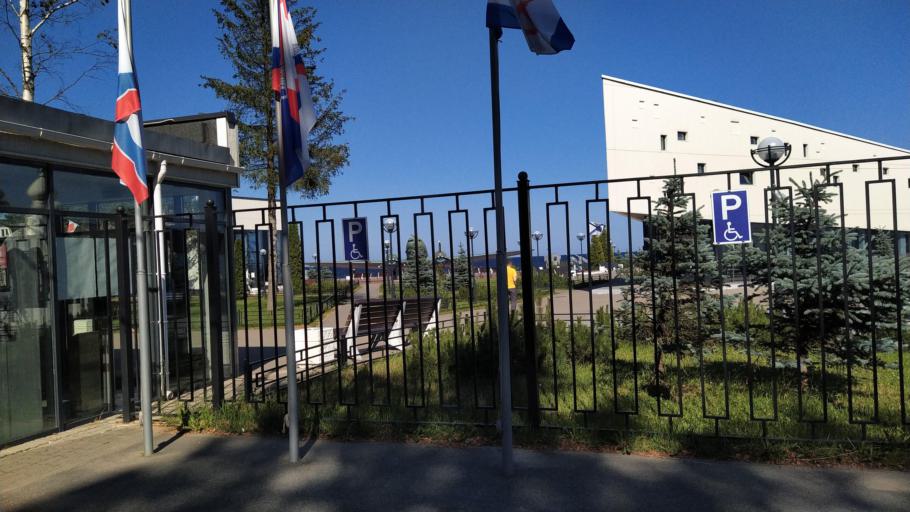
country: RU
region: Leningrad
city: Borisova Griva
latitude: 60.1241
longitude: 31.0747
